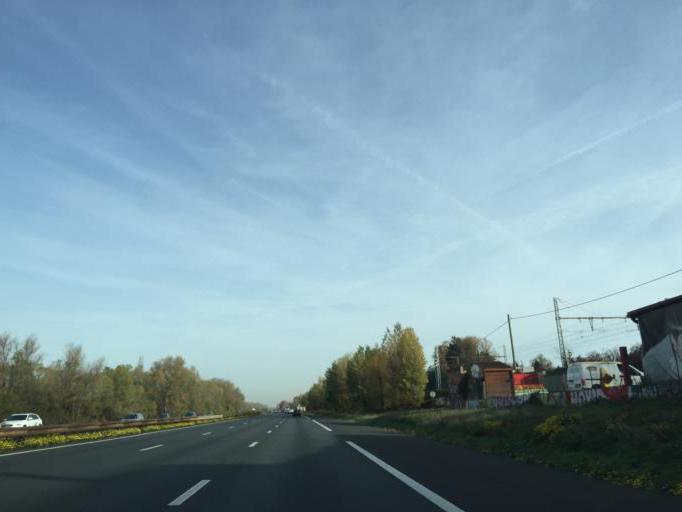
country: FR
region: Rhone-Alpes
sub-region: Departement du Rhone
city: Ternay
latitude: 45.6181
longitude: 4.8119
